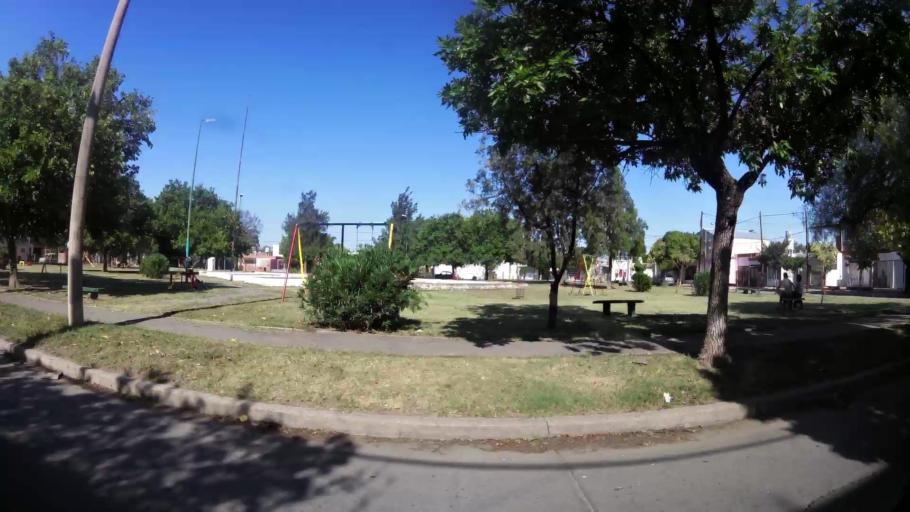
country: AR
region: Cordoba
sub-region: Departamento de Capital
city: Cordoba
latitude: -31.3920
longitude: -64.1341
